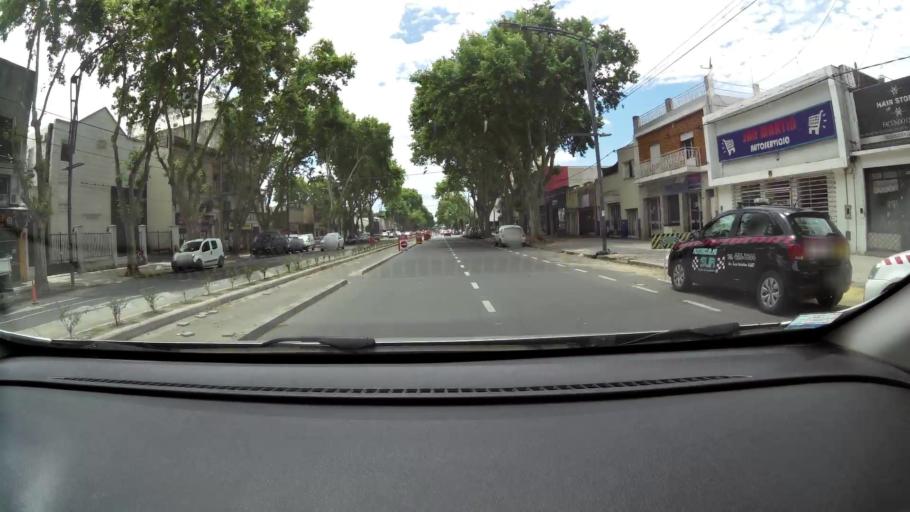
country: AR
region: Santa Fe
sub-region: Departamento de Rosario
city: Rosario
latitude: -32.9884
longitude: -60.6461
